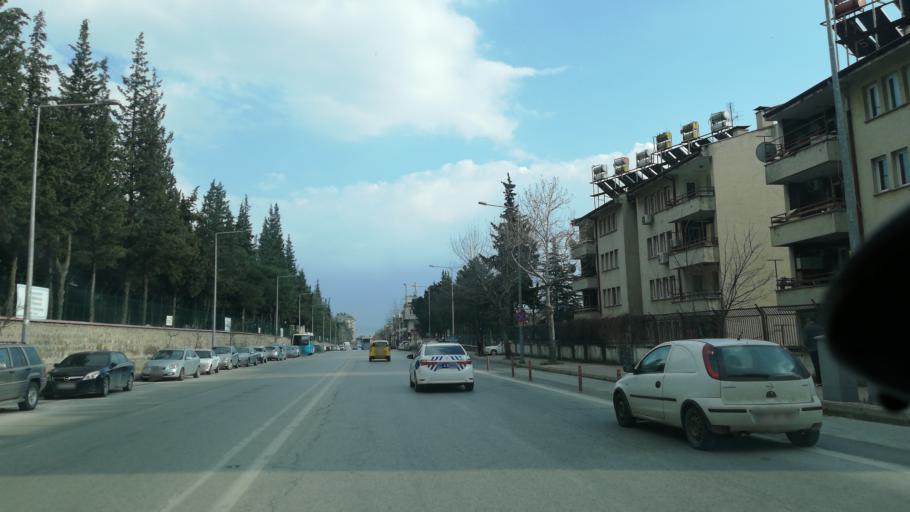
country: TR
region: Kahramanmaras
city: Kahramanmaras
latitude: 37.5762
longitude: 36.9349
